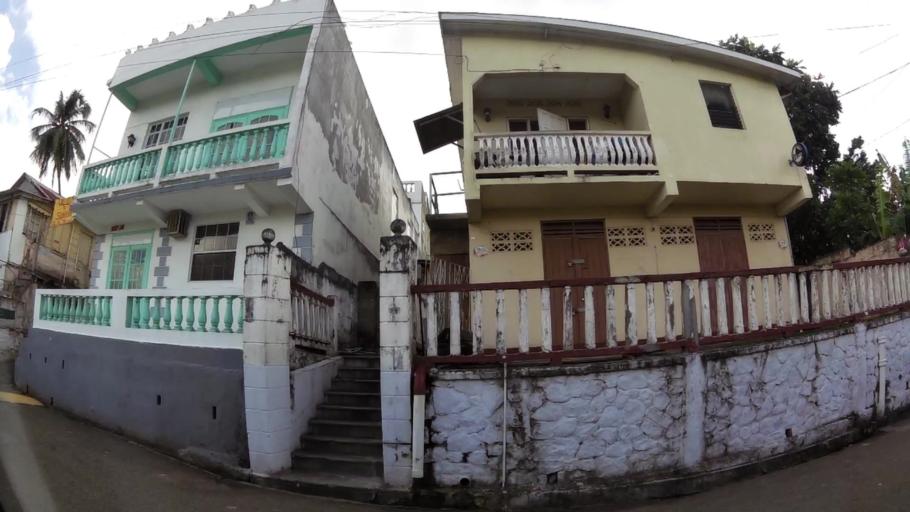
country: LC
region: Castries Quarter
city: Castries
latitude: 14.0040
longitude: -60.9857
